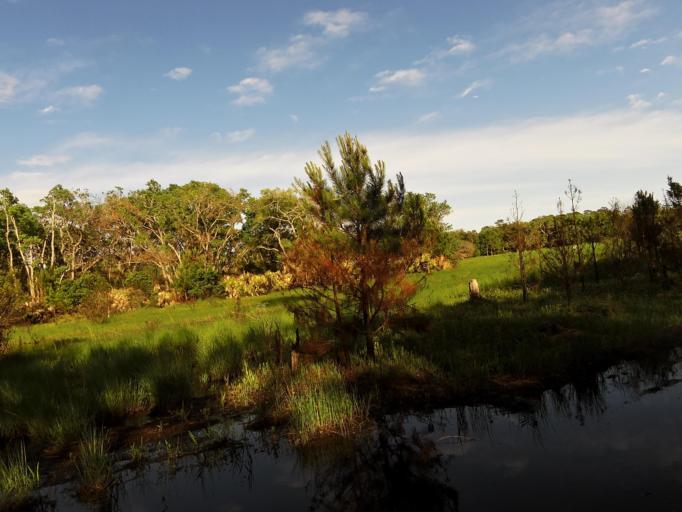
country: US
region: Florida
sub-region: Saint Johns County
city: Villano Beach
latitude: 30.0231
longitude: -81.3380
